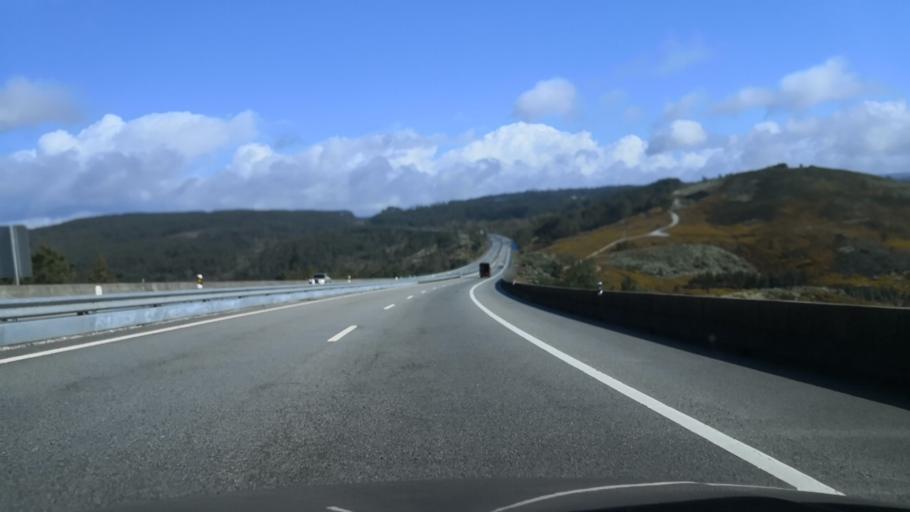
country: PT
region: Viseu
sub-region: Viseu
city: Campo
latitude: 40.7466
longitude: -7.9244
